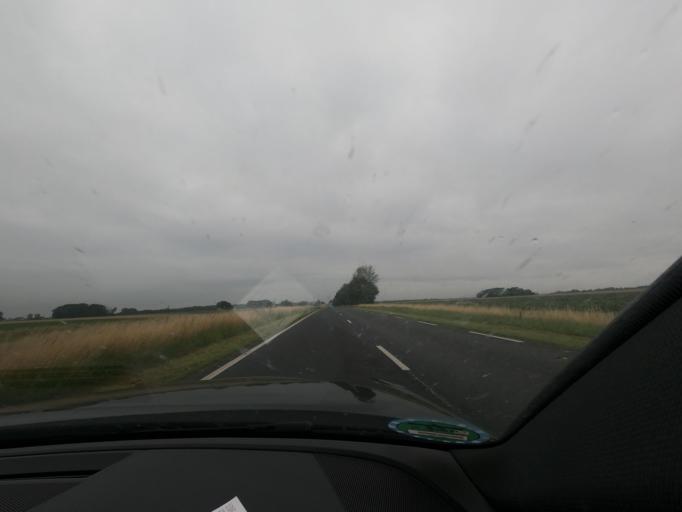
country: FR
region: Picardie
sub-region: Departement de la Somme
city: Harbonnieres
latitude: 49.7780
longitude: 2.5994
